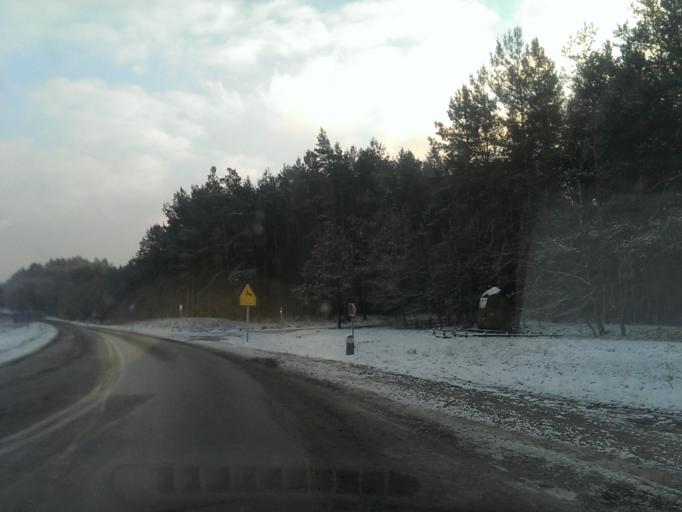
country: PL
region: Kujawsko-Pomorskie
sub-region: Powiat sepolenski
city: Wiecbork
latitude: 53.3418
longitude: 17.4780
